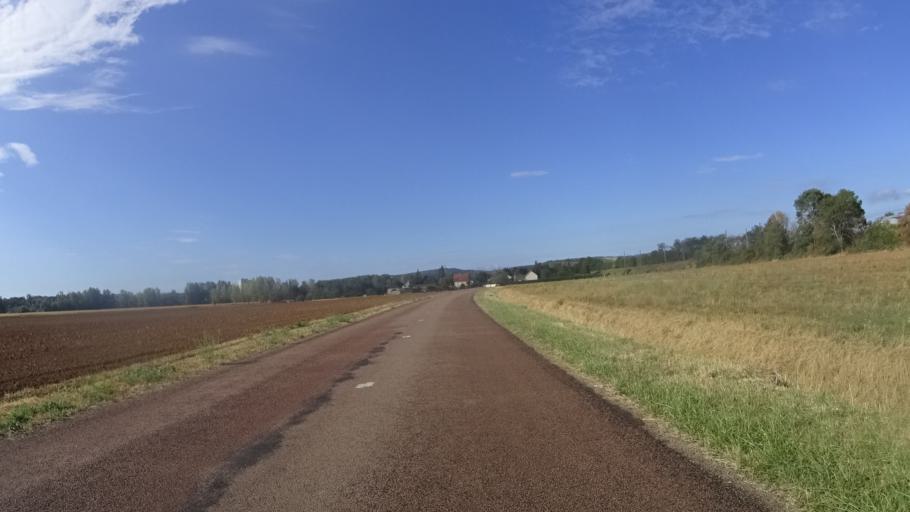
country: FR
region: Bourgogne
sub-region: Departement de la Cote-d'Or
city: Corpeau
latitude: 46.9231
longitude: 4.7592
